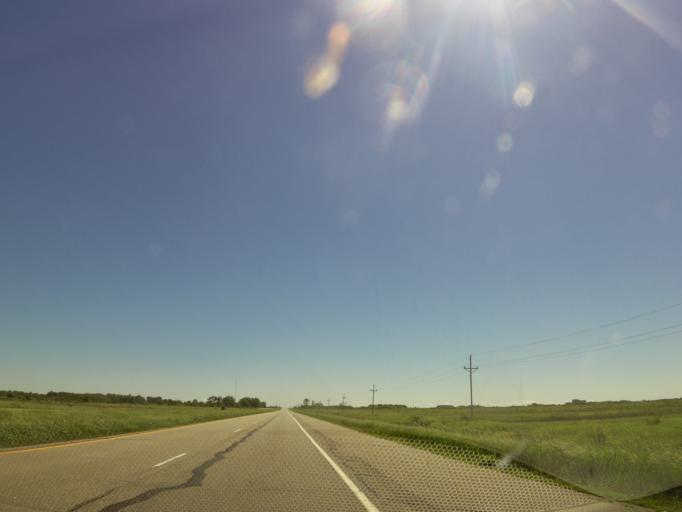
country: US
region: Minnesota
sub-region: Red Lake County
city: Red Lake Falls
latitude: 47.7606
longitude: -96.3653
